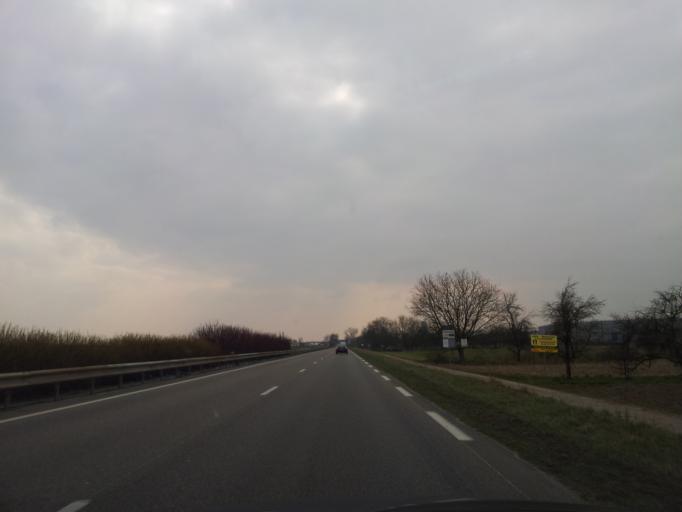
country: FR
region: Alsace
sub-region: Departement du Bas-Rhin
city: Erstein
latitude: 48.4309
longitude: 7.6445
